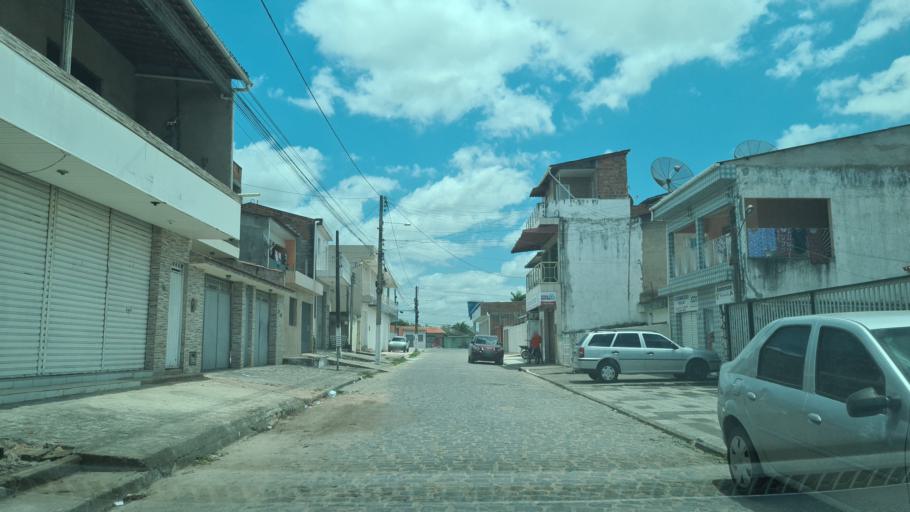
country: BR
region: Alagoas
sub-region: Uniao Dos Palmares
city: Uniao dos Palmares
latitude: -9.1646
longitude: -36.0226
